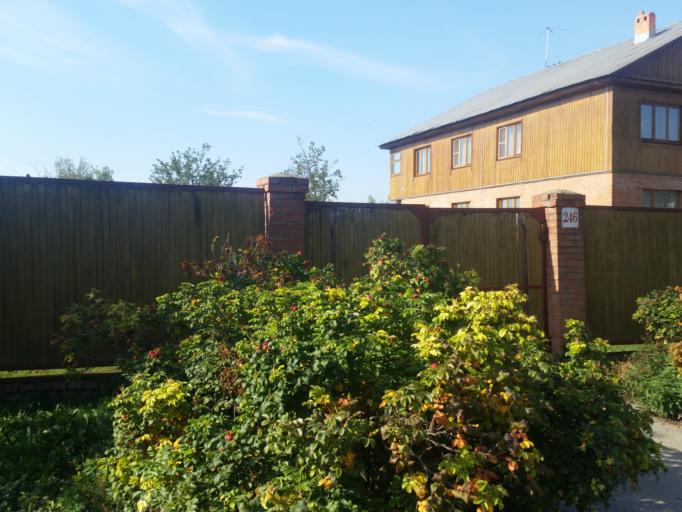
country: RU
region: Ulyanovsk
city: Dimitrovgrad
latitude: 54.2286
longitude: 49.6100
